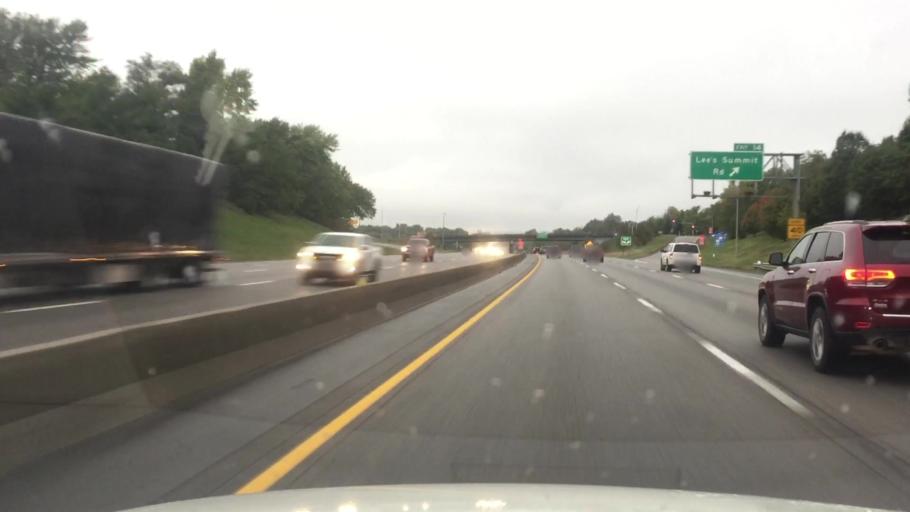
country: US
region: Missouri
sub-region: Jackson County
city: Independence
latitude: 39.0447
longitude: -94.3831
